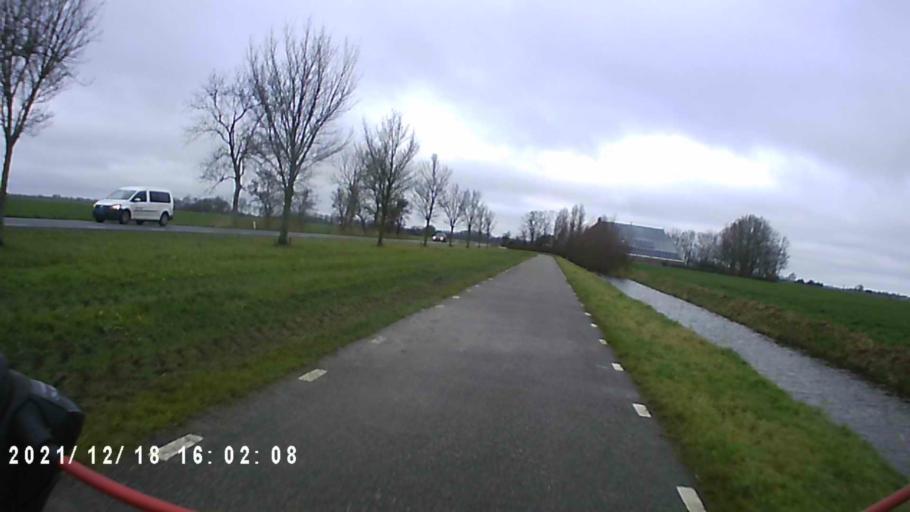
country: NL
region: Friesland
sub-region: Gemeente Dongeradeel
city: Anjum
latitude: 53.3465
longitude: 6.0845
